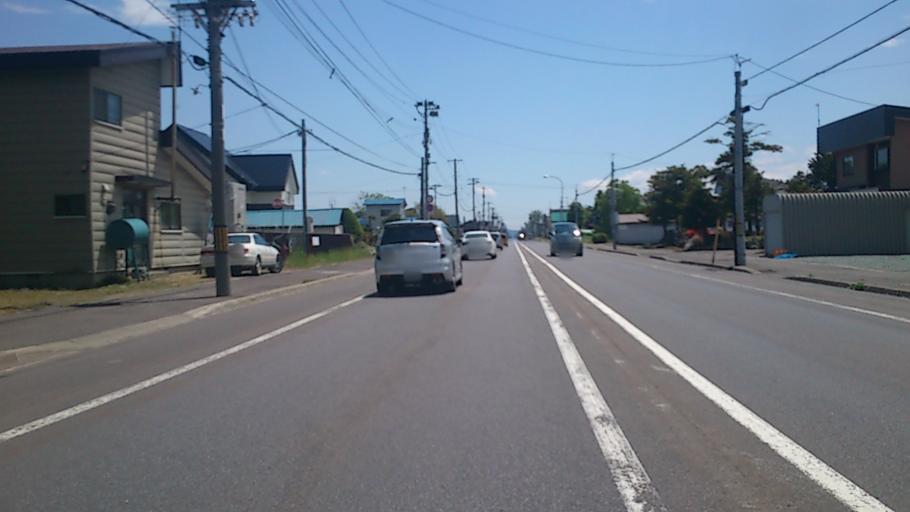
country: JP
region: Hokkaido
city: Nayoro
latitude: 44.2455
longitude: 142.3949
